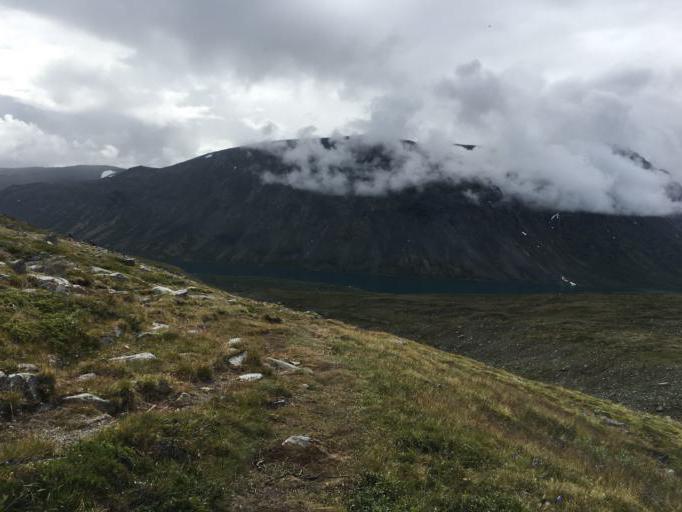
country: NO
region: Oppland
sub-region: Lom
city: Fossbergom
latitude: 61.5716
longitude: 8.6735
